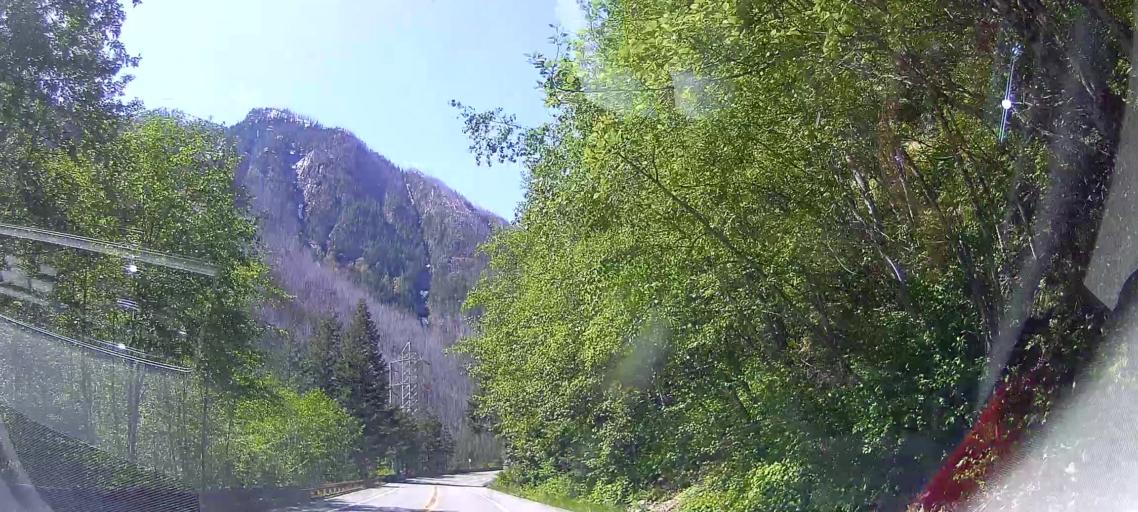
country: US
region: Washington
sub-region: Snohomish County
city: Darrington
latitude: 48.7025
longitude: -121.1918
